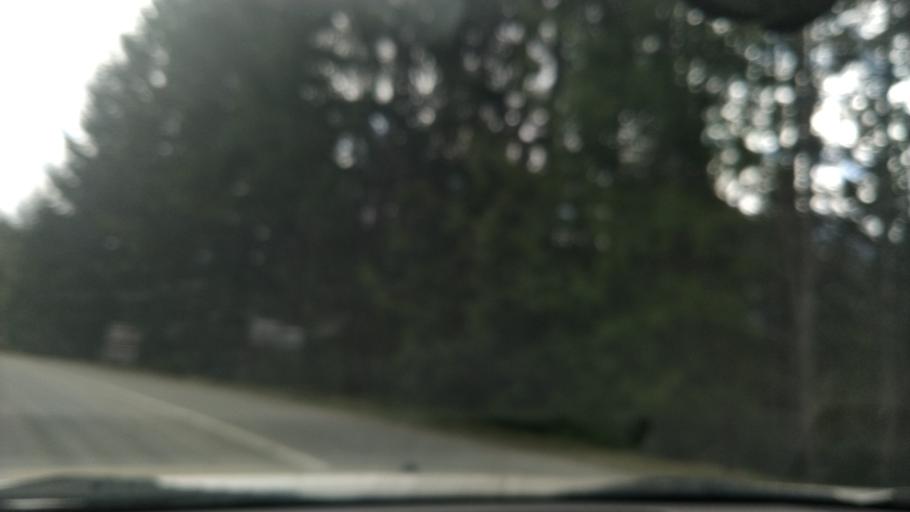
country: CA
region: British Columbia
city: Campbell River
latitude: 49.8372
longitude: -125.6313
